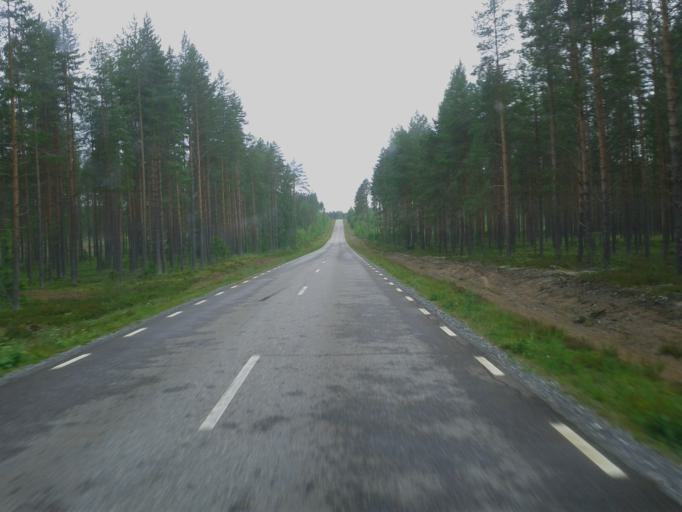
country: SE
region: Vaesterbotten
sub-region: Skelleftea Kommun
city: Kage
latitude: 64.9185
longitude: 20.9257
